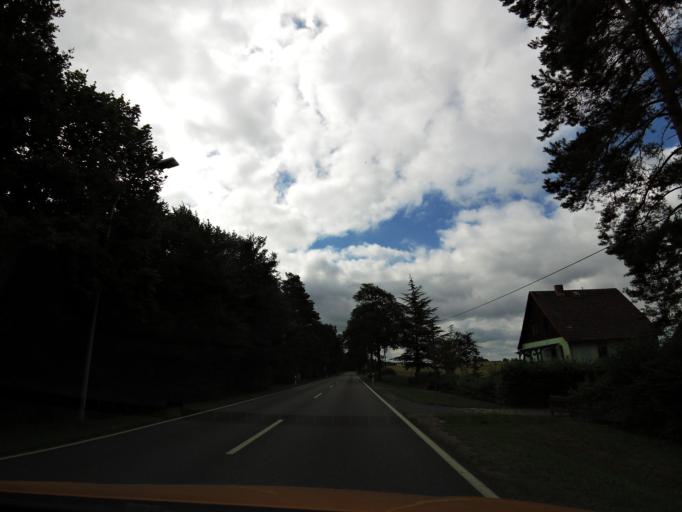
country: DE
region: Mecklenburg-Vorpommern
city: Muhl Rosin
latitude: 53.7718
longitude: 12.2441
